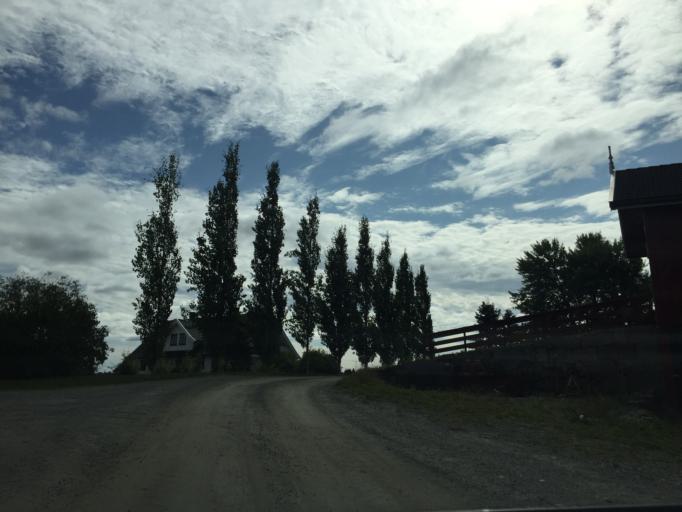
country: NO
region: Ostfold
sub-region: Hobol
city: Elvestad
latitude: 59.6344
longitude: 10.8862
